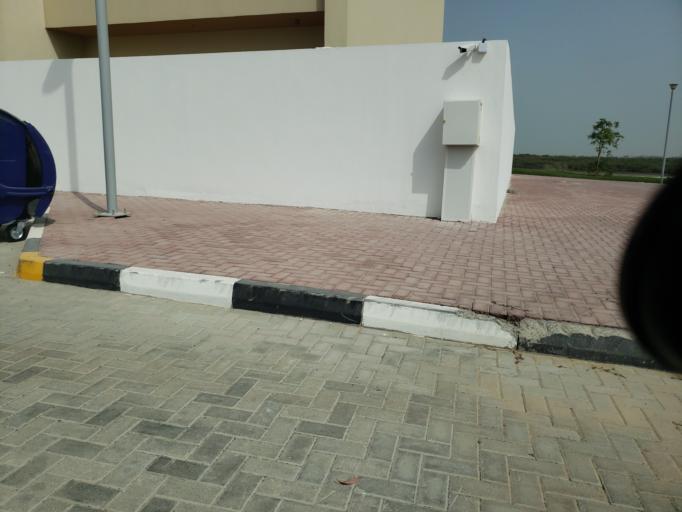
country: AE
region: Ajman
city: Ajman
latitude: 25.4233
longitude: 55.4937
